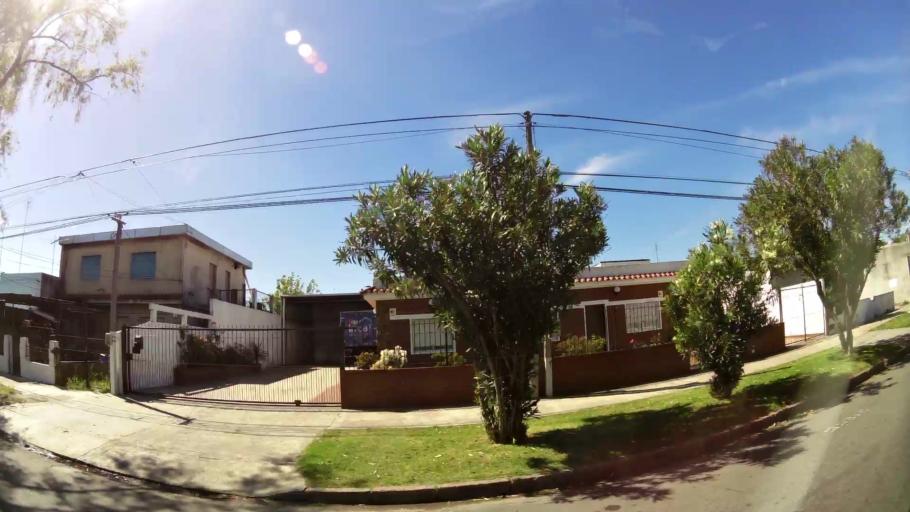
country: UY
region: Canelones
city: Paso de Carrasco
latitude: -34.8651
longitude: -56.1177
